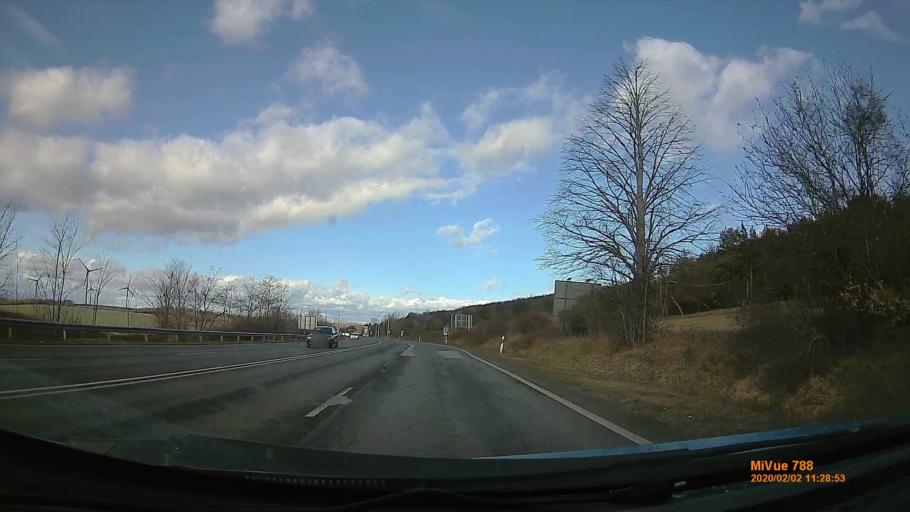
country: AT
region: Burgenland
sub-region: Eisenstadt-Umgebung
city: Klingenbach
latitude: 47.7321
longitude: 16.5547
